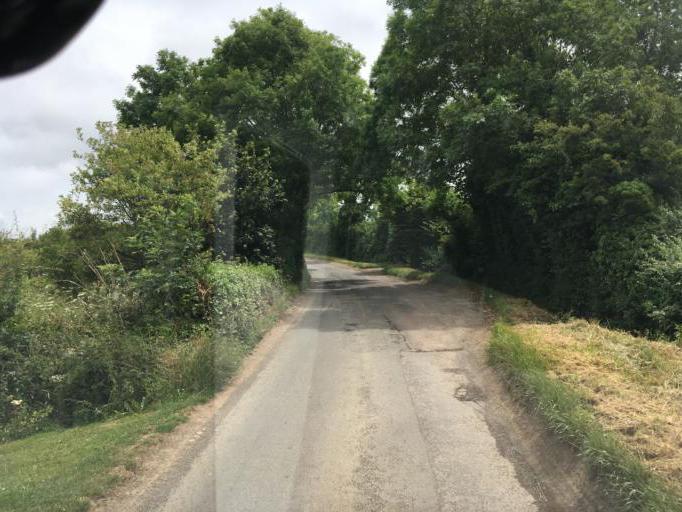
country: GB
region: England
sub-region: Gloucestershire
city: Stonehouse
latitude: 51.7034
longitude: -2.2708
